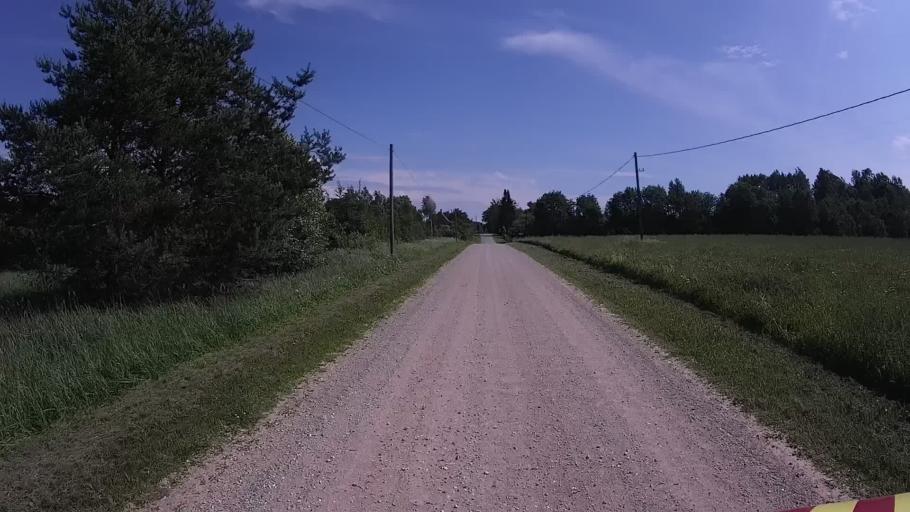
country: EE
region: Viljandimaa
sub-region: Karksi vald
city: Karksi-Nuia
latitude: 57.9965
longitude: 25.5332
